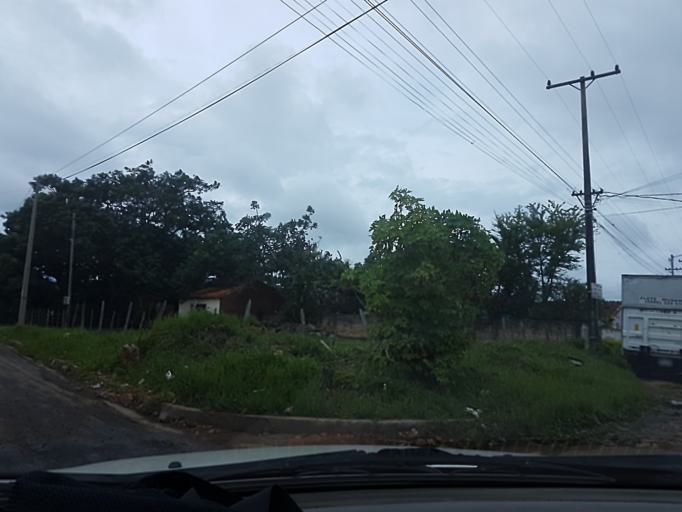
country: PY
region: Central
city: Limpio
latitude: -25.1766
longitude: -57.4824
